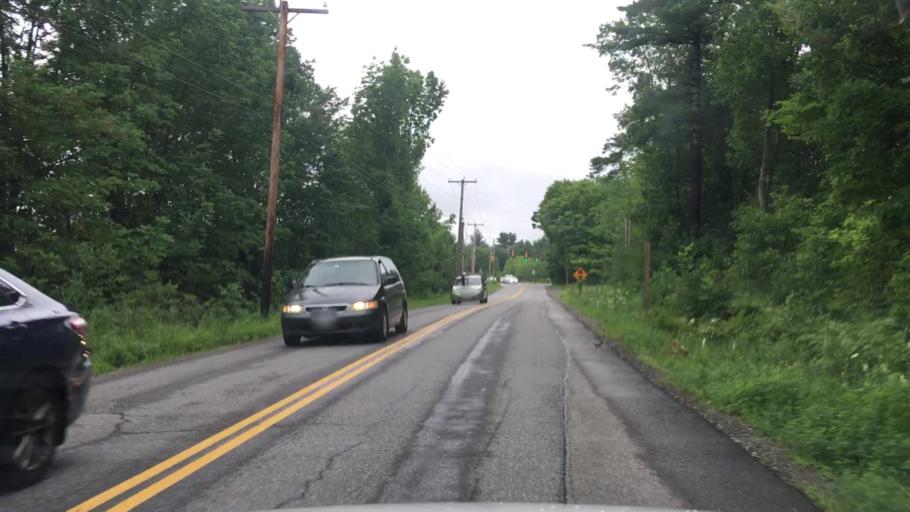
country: US
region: Maine
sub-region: Kennebec County
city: Augusta
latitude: 44.3195
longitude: -69.7353
